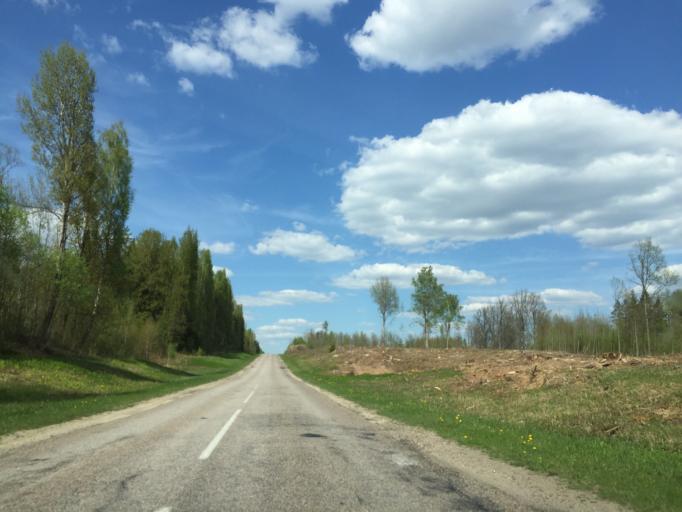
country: LV
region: Limbazu Rajons
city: Limbazi
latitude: 57.4081
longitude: 24.6924
